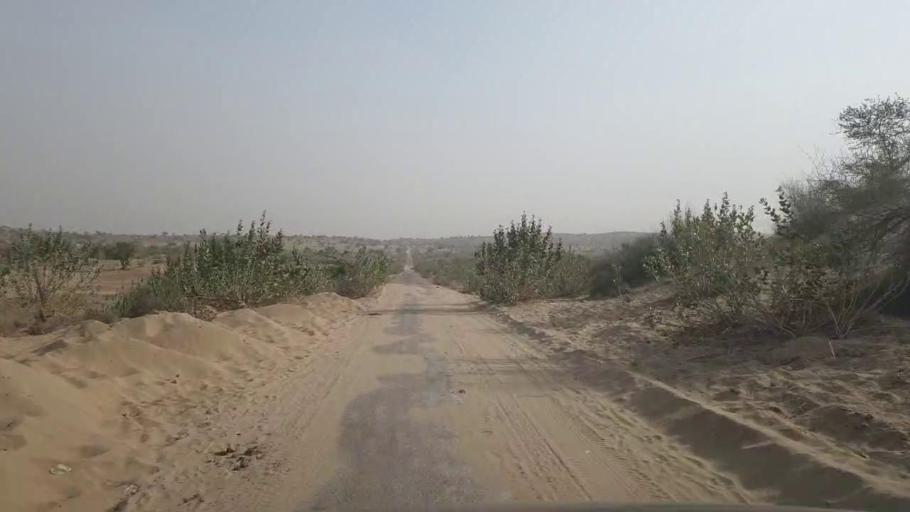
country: PK
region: Sindh
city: Chor
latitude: 25.5222
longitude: 69.9628
